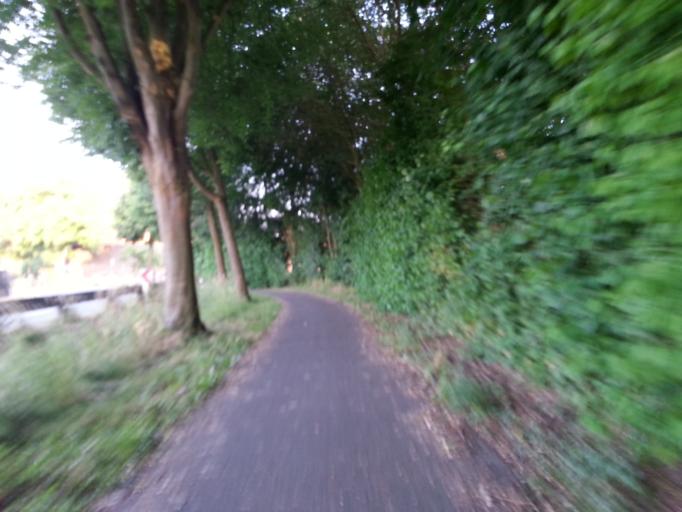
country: DE
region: North Rhine-Westphalia
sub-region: Regierungsbezirk Munster
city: Havixbeck
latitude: 51.9634
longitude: 7.4153
